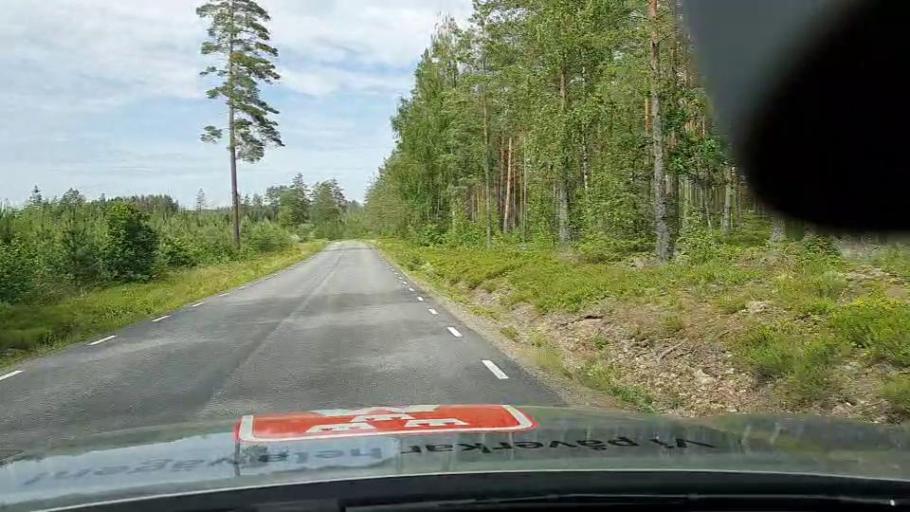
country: SE
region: Soedermanland
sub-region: Eskilstuna Kommun
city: Arla
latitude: 59.2349
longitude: 16.7232
